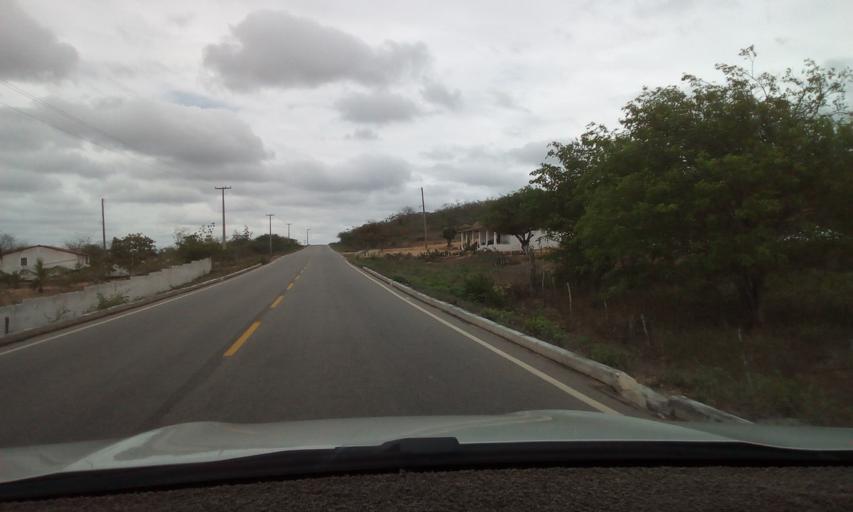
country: BR
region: Paraiba
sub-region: Picui
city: Picui
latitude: -6.5737
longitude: -36.2666
